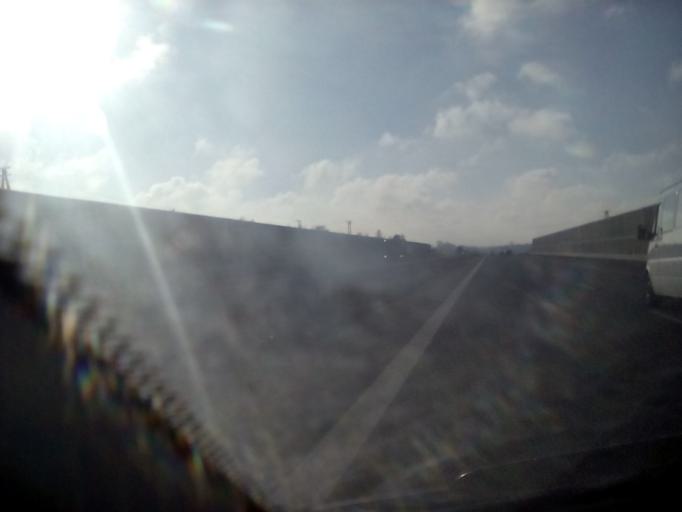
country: PL
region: Masovian Voivodeship
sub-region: Powiat grojecki
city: Grojec
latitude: 51.8138
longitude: 20.8844
